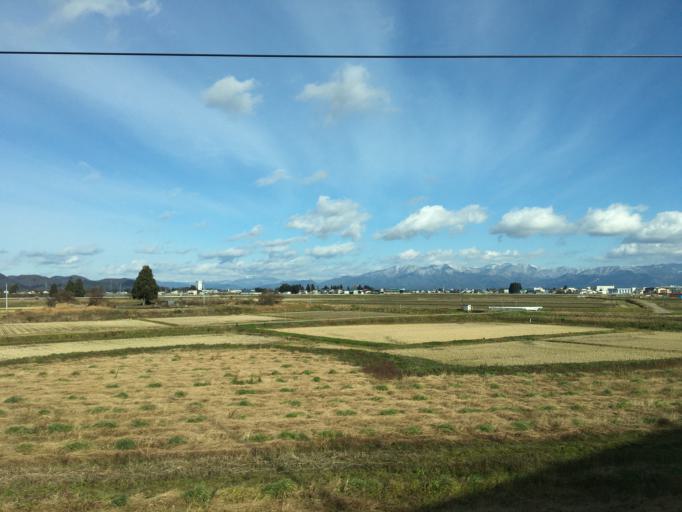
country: JP
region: Akita
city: Omagari
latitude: 39.4768
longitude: 140.4681
